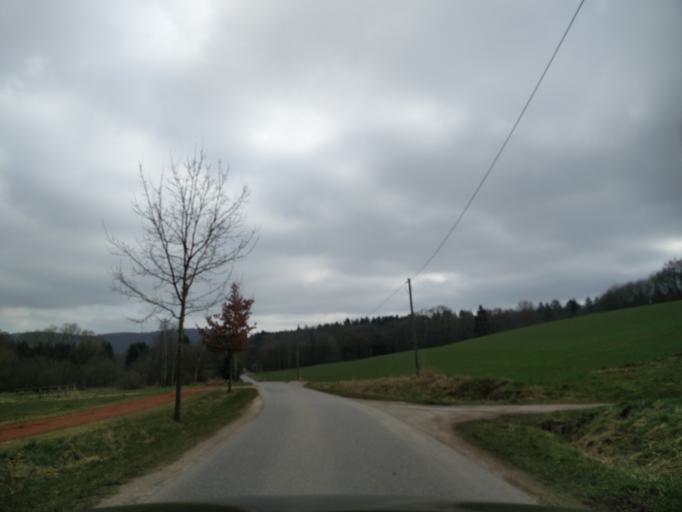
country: DE
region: North Rhine-Westphalia
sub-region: Regierungsbezirk Detmold
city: Willebadessen
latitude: 51.5245
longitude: 9.0022
